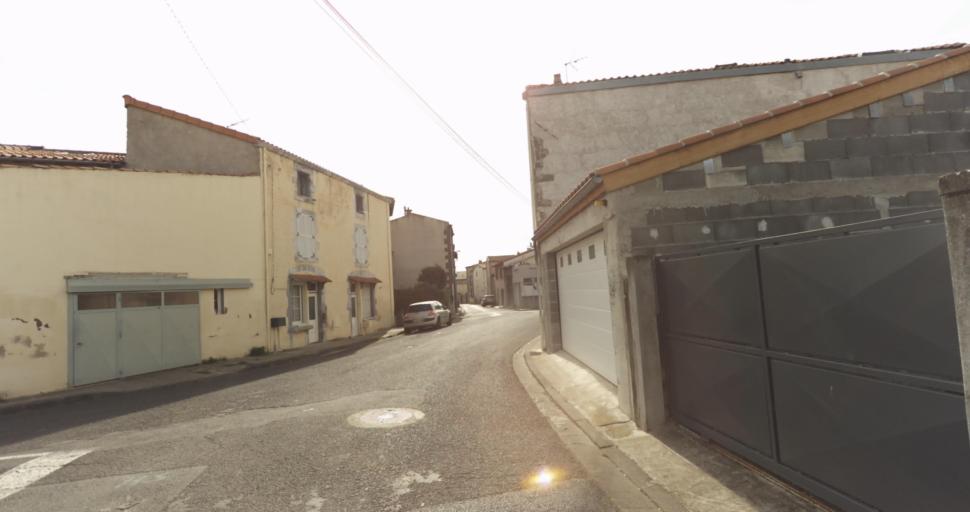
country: FR
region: Auvergne
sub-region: Departement du Puy-de-Dome
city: Cebazat
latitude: 45.8320
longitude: 3.1014
